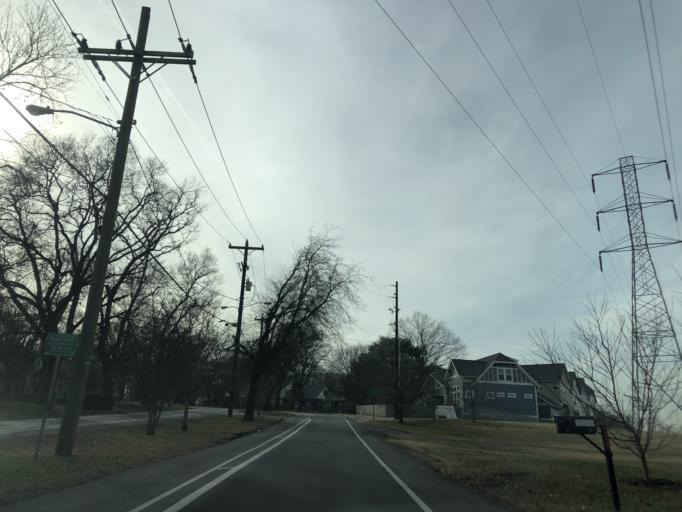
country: US
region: Tennessee
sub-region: Davidson County
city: Nashville
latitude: 36.2067
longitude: -86.7234
